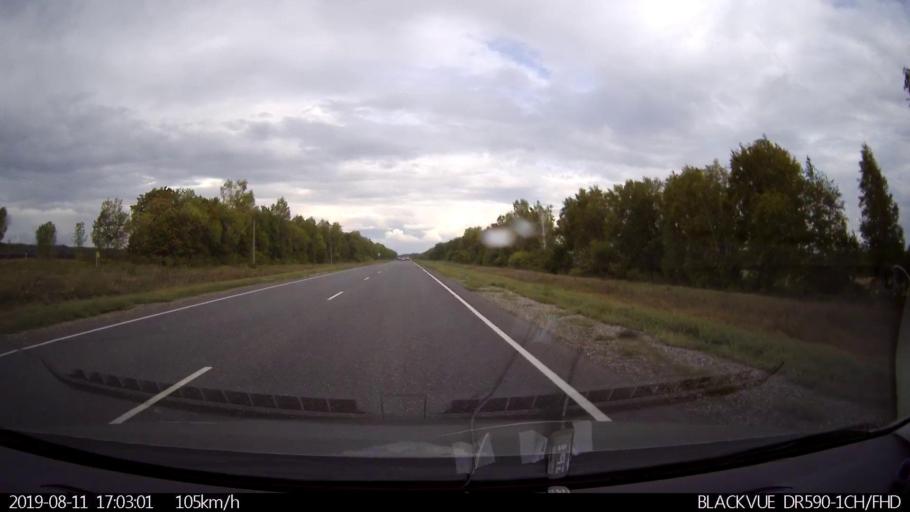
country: RU
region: Ulyanovsk
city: Mayna
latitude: 54.3043
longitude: 47.7291
